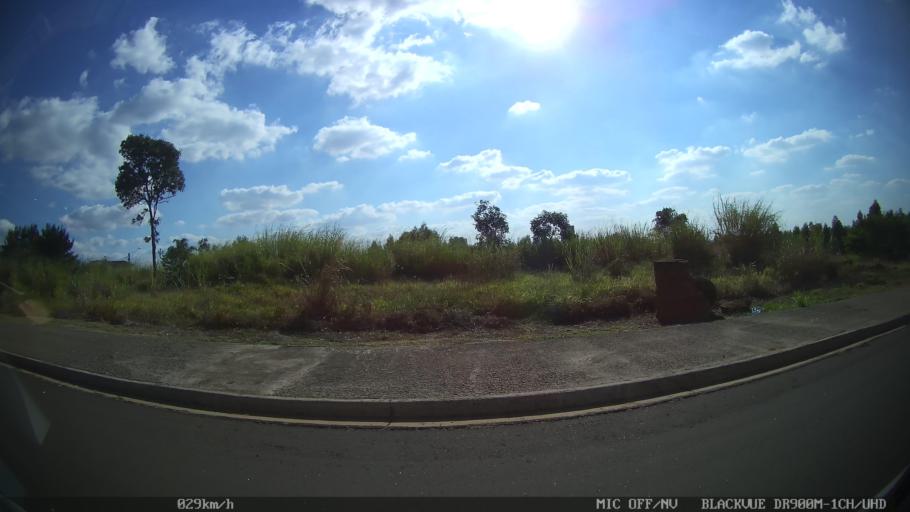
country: BR
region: Sao Paulo
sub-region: Nova Odessa
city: Nova Odessa
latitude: -22.7843
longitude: -47.3039
